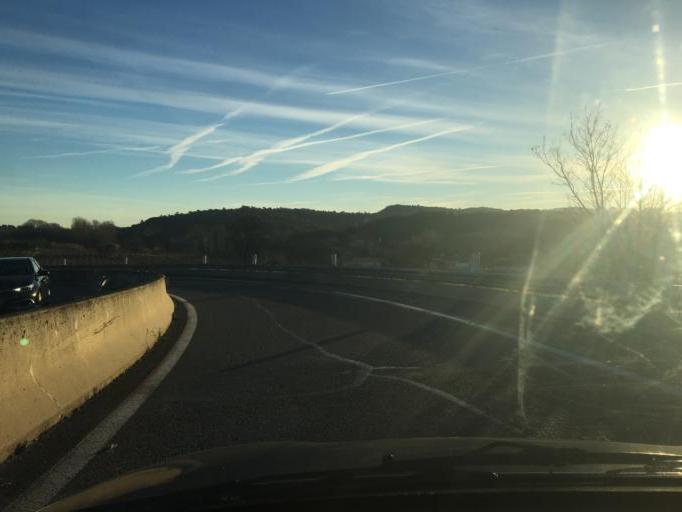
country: FR
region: Provence-Alpes-Cote d'Azur
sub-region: Departement du Var
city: Les Arcs
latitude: 43.4493
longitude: 6.4931
